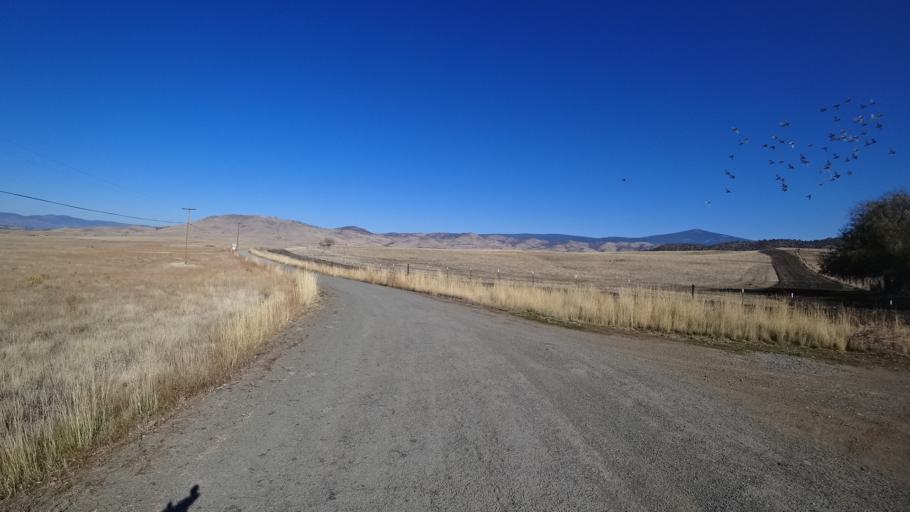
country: US
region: California
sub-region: Siskiyou County
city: Montague
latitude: 41.7943
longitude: -122.4176
